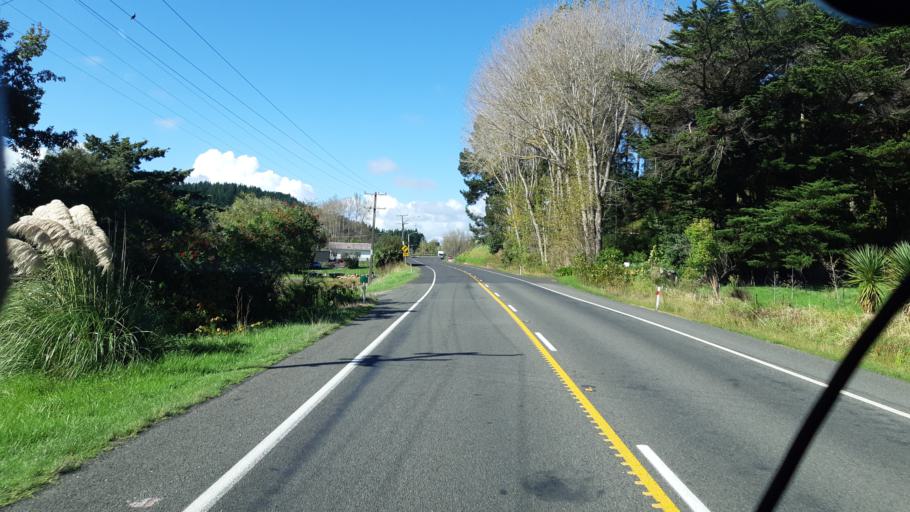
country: NZ
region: Manawatu-Wanganui
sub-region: Wanganui District
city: Wanganui
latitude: -39.9601
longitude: 175.0951
